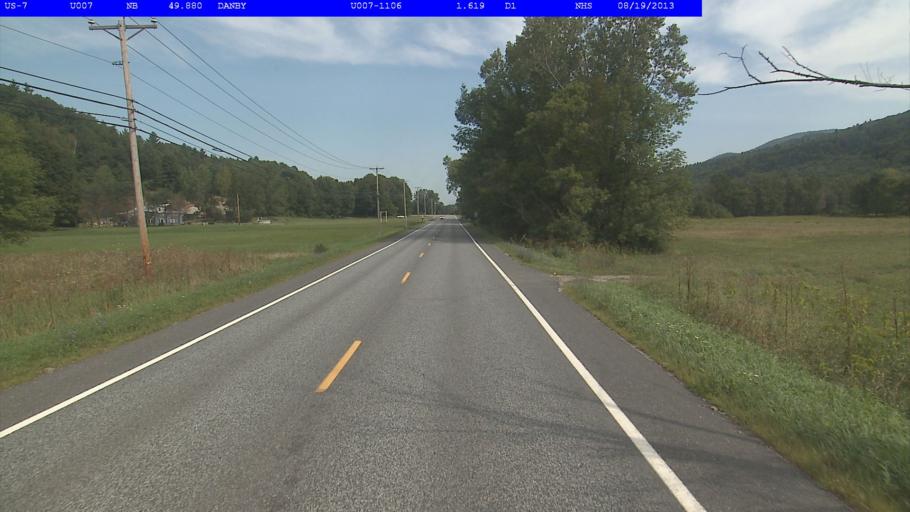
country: US
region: Vermont
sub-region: Rutland County
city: West Rutland
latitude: 43.3852
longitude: -72.9981
